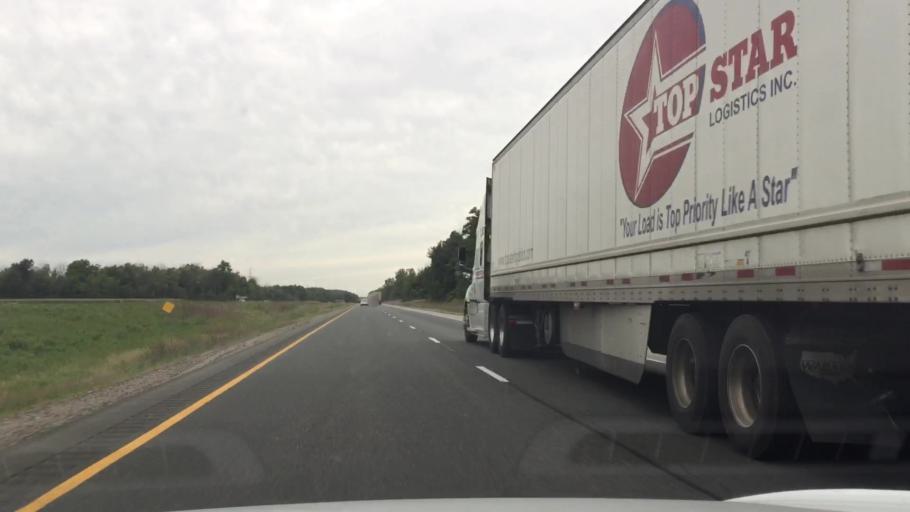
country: CA
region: Ontario
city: Lambton Shores
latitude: 42.9924
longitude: -81.7624
